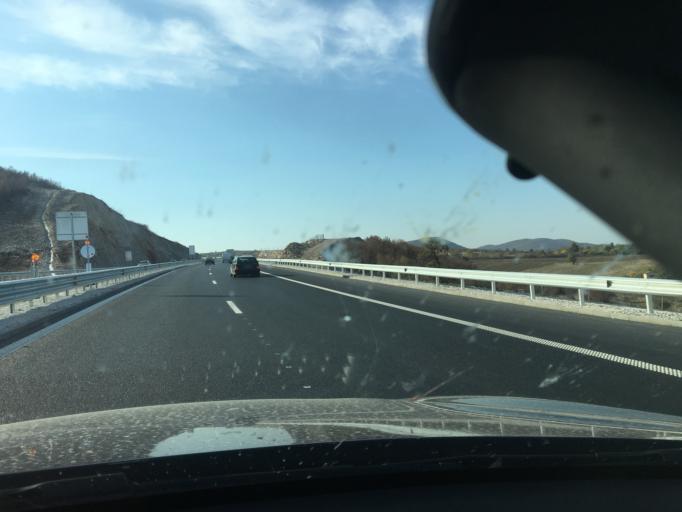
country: BG
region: Lovech
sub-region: Obshtina Yablanitsa
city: Yablanitsa
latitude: 43.0527
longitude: 24.2116
